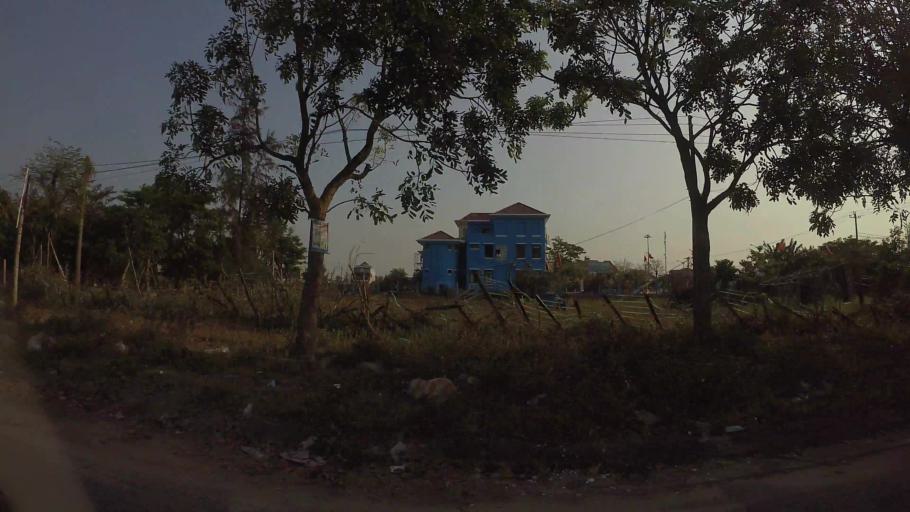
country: VN
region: Da Nang
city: Ngu Hanh Son
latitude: 15.9577
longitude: 108.2553
